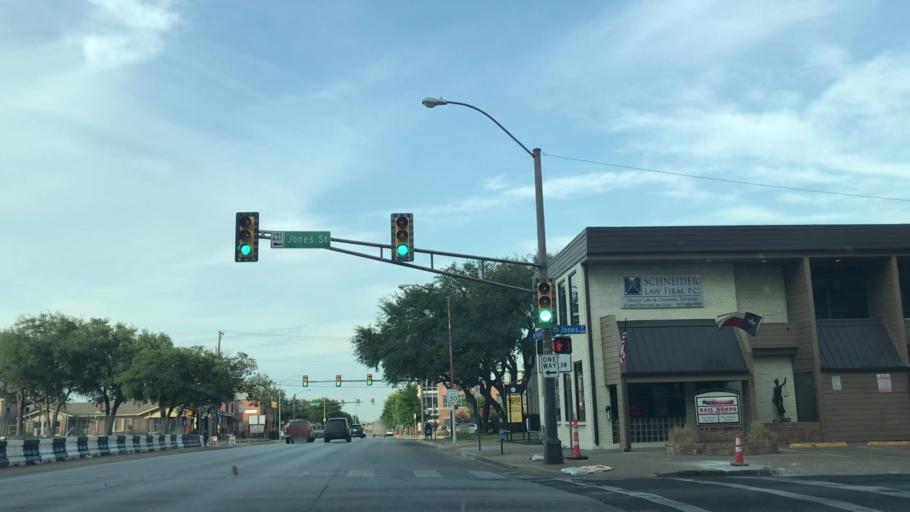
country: US
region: Texas
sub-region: Tarrant County
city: Fort Worth
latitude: 32.7581
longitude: -97.3307
